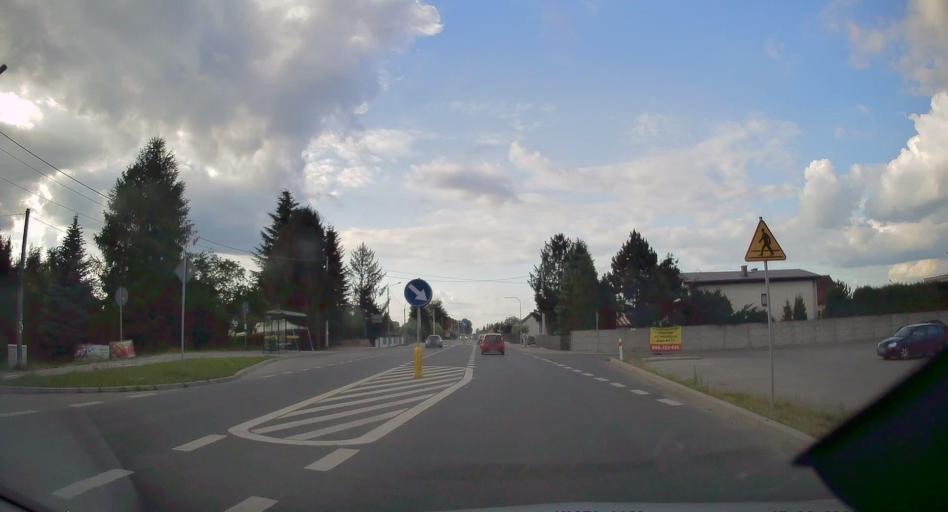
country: PL
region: Lesser Poland Voivodeship
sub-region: Powiat oswiecimski
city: Nowa Wies
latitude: 49.9037
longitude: 19.2172
